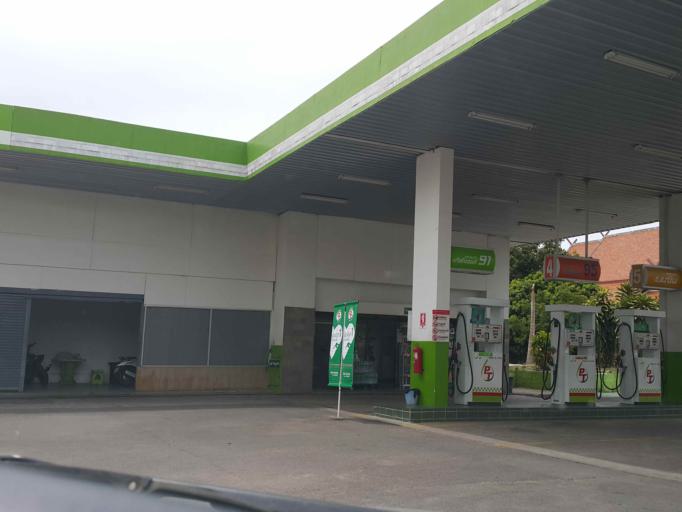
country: TH
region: Chiang Mai
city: Chiang Mai
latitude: 18.7399
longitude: 98.9576
